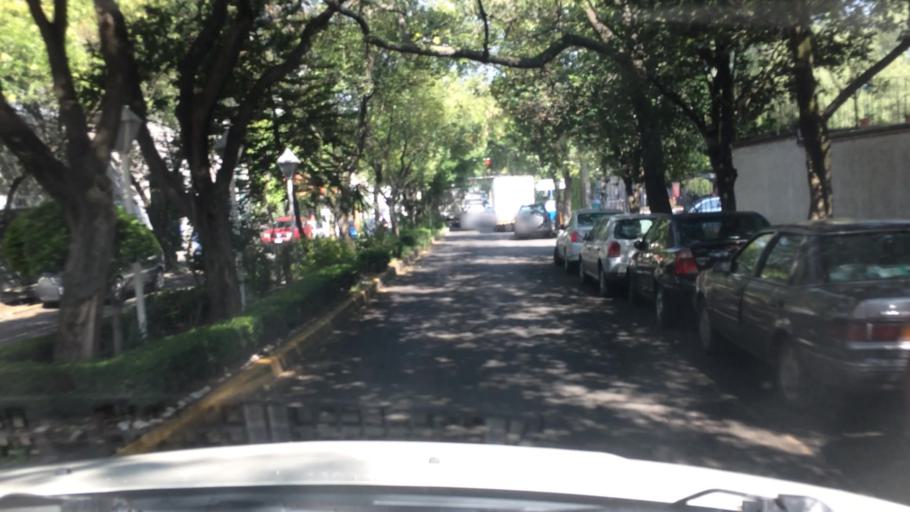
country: MX
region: Mexico City
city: Tlalpan
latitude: 19.2818
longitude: -99.1640
